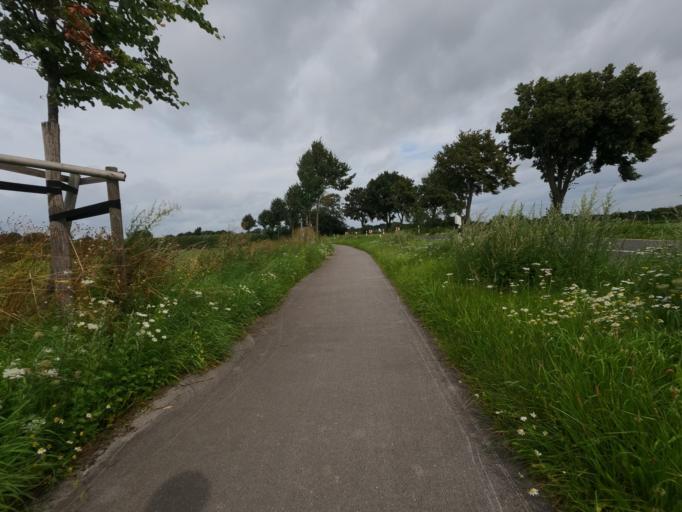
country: DE
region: North Rhine-Westphalia
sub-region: Regierungsbezirk Koln
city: Heinsberg
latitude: 51.0322
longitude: 6.1544
